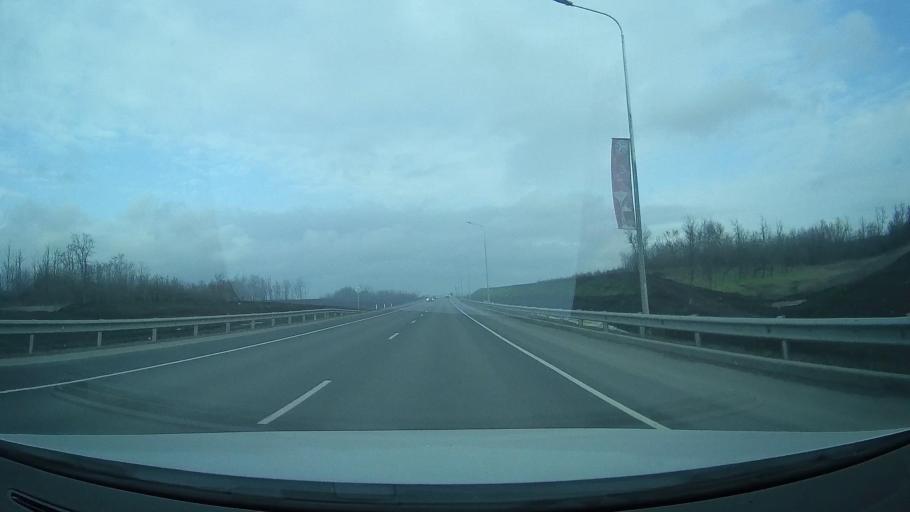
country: RU
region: Rostov
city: Grushevskaya
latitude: 47.4191
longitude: 39.8622
